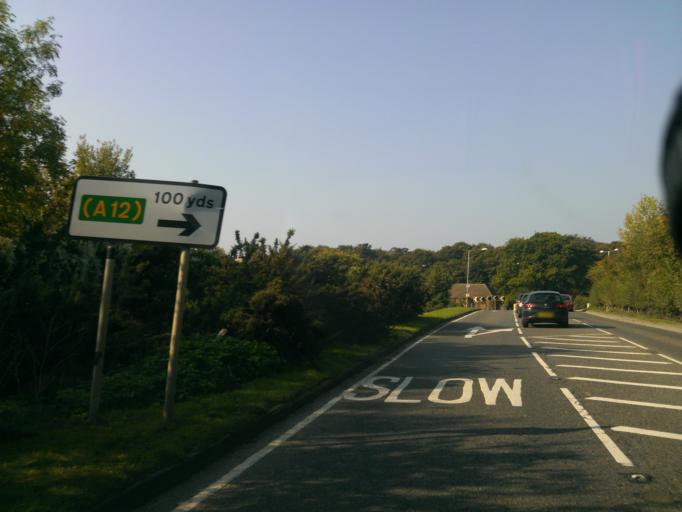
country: GB
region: England
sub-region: Essex
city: Eight Ash Green
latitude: 51.8631
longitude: 0.8280
